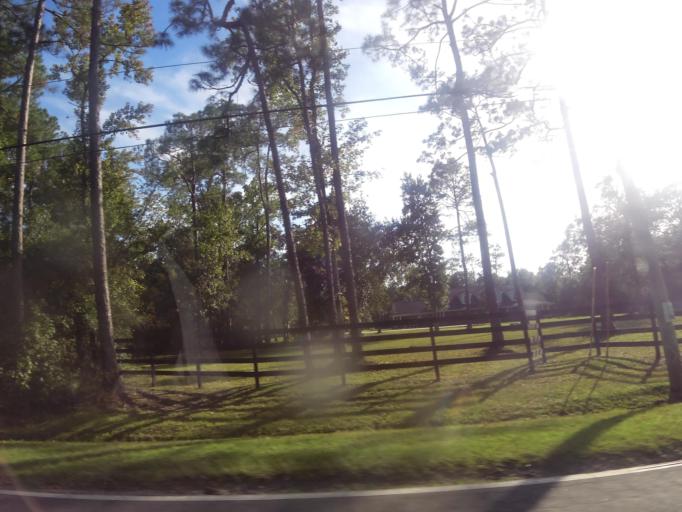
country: US
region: Florida
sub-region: Clay County
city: Green Cove Springs
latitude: 29.9162
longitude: -81.5407
